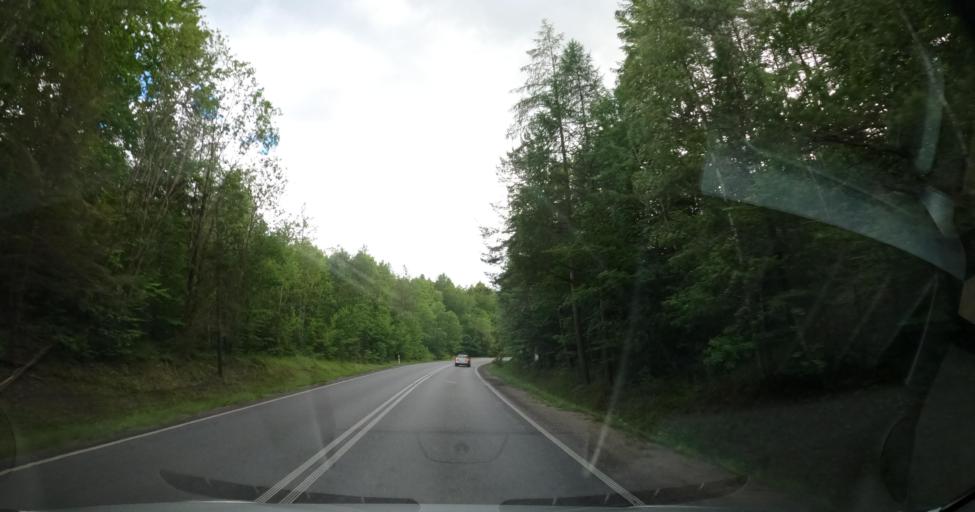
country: PL
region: Pomeranian Voivodeship
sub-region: Powiat kartuski
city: Sierakowice
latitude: 54.3403
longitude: 17.9951
